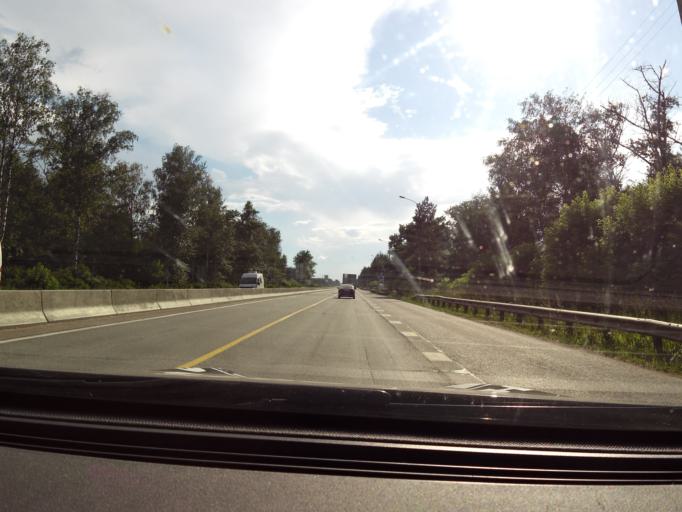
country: RU
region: Nizjnij Novgorod
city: Mulino
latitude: 56.2658
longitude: 42.9339
